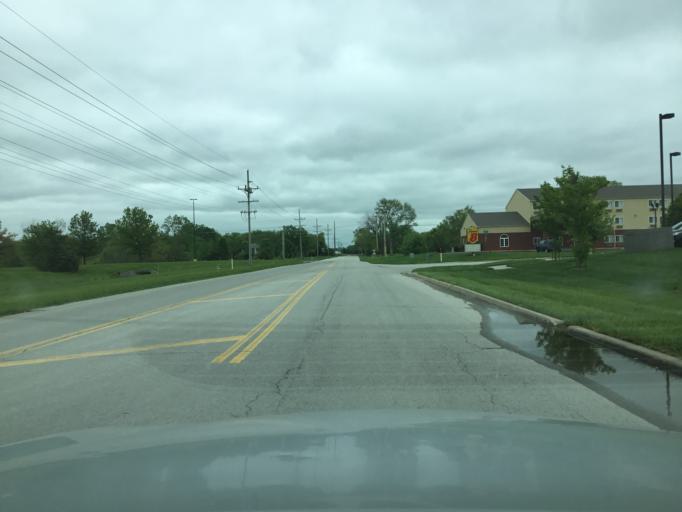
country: US
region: Kansas
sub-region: Franklin County
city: Ottawa
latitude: 38.5793
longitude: -95.2651
